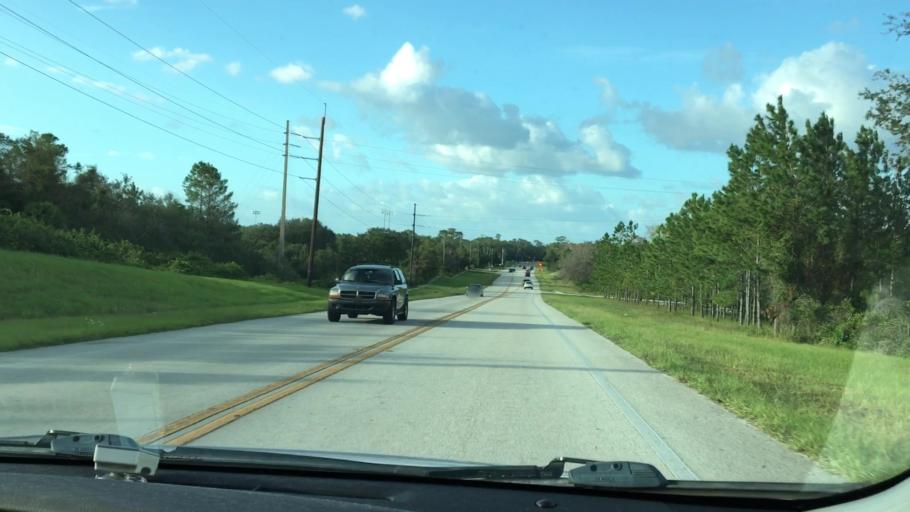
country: US
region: Florida
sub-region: Volusia County
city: Orange City
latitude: 28.9290
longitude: -81.2819
